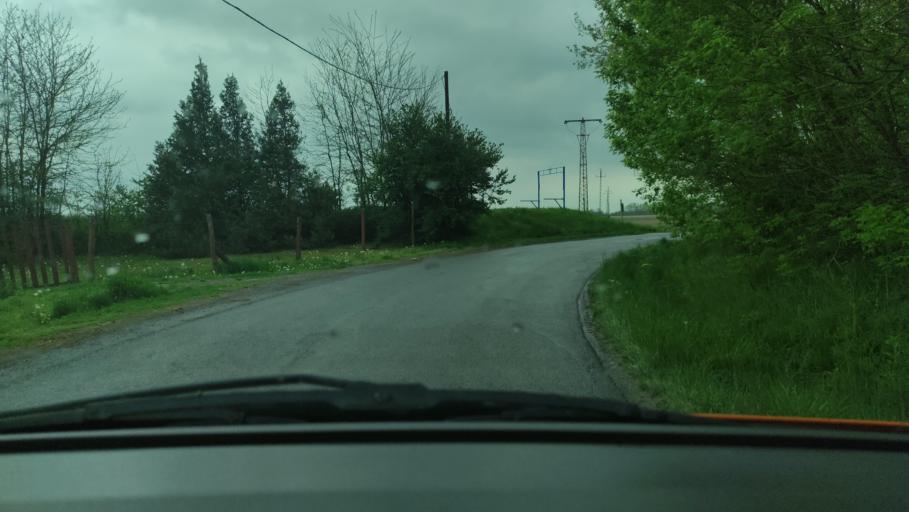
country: HU
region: Baranya
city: Mohacs
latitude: 45.9285
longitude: 18.7061
